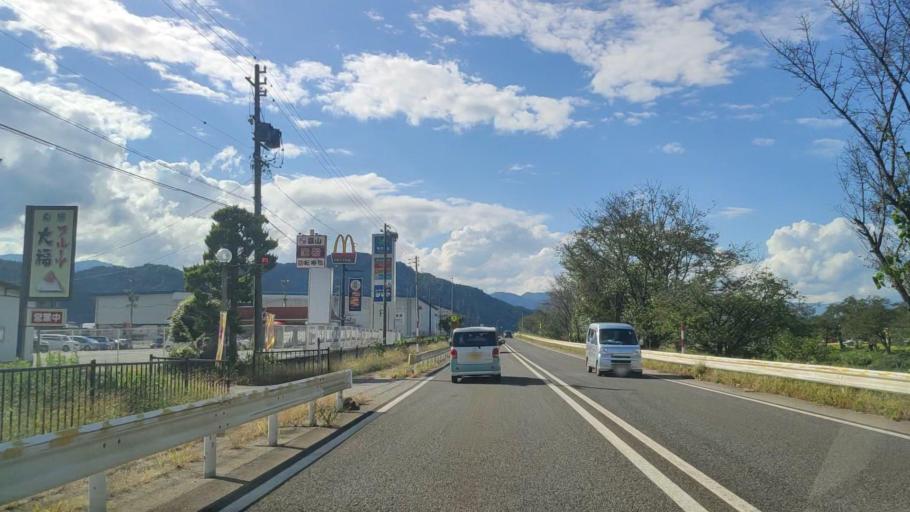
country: JP
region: Gifu
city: Takayama
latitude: 36.2056
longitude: 137.2231
